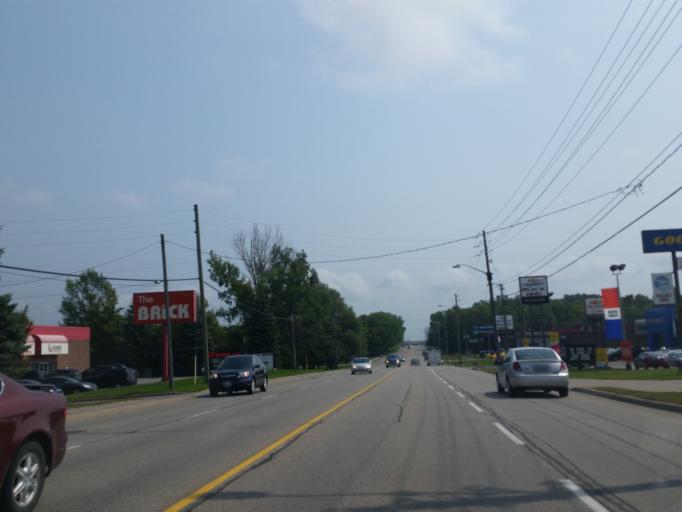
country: CA
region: Ontario
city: Brockville
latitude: 44.6034
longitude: -75.7130
